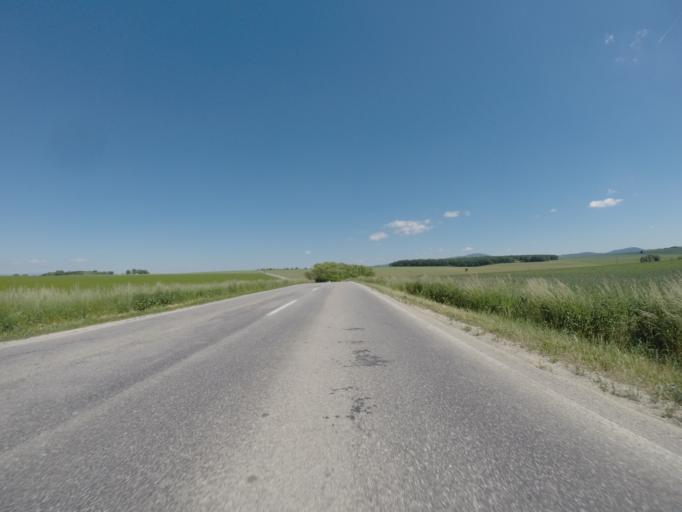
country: SK
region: Nitriansky
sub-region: Okres Nitra
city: Nitra
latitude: 48.5261
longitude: 18.0720
